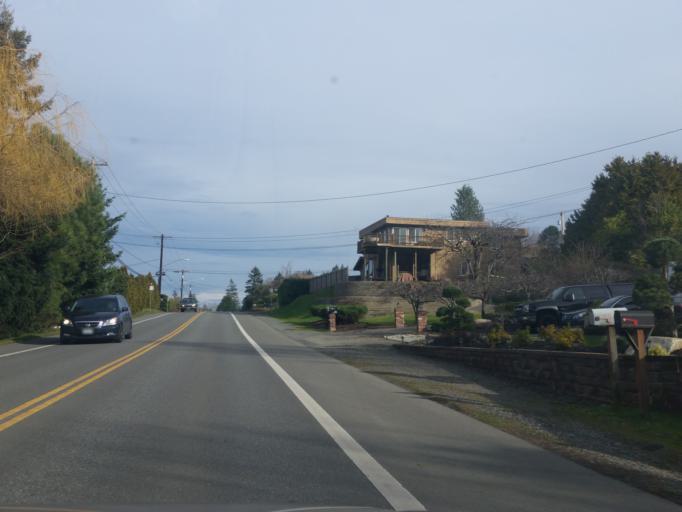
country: US
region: Washington
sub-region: Snohomish County
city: Mukilteo
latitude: 47.9523
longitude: -122.2820
